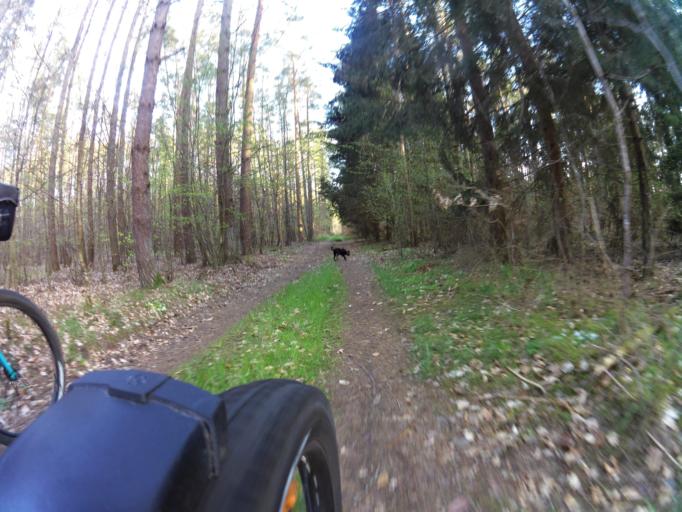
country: PL
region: West Pomeranian Voivodeship
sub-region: Powiat gryficki
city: Ploty
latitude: 53.7521
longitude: 15.2878
